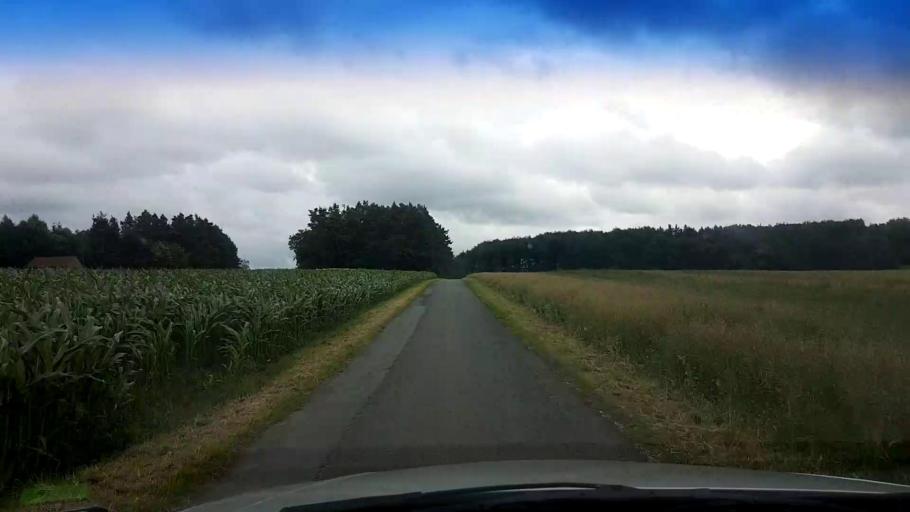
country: DE
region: Bavaria
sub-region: Upper Franconia
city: Poxdorf
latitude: 49.9020
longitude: 11.0811
